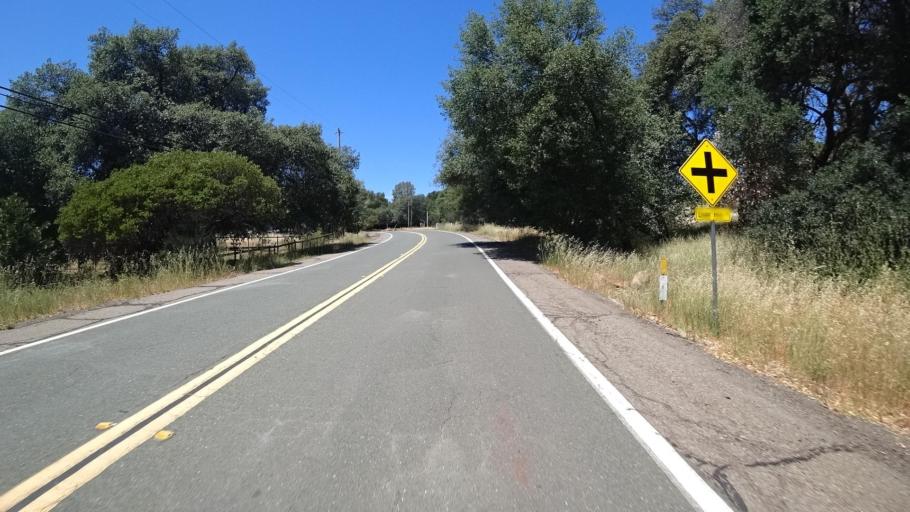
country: US
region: California
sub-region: Lake County
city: Hidden Valley Lake
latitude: 38.8198
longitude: -122.5701
